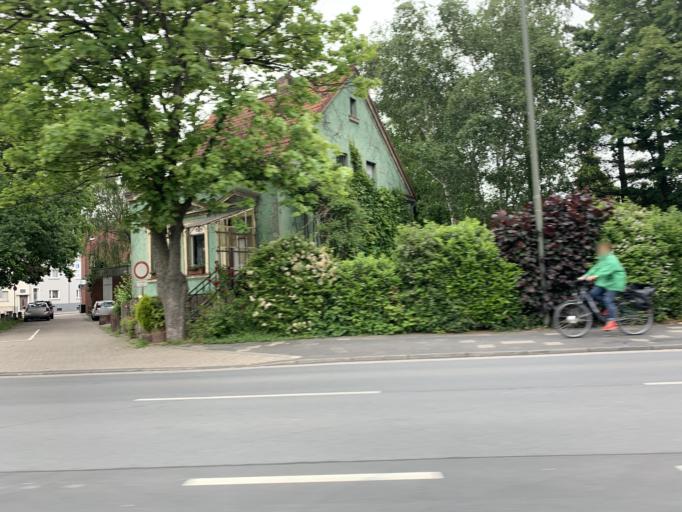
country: DE
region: North Rhine-Westphalia
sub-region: Regierungsbezirk Arnsberg
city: Hamm
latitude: 51.6716
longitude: 7.8174
